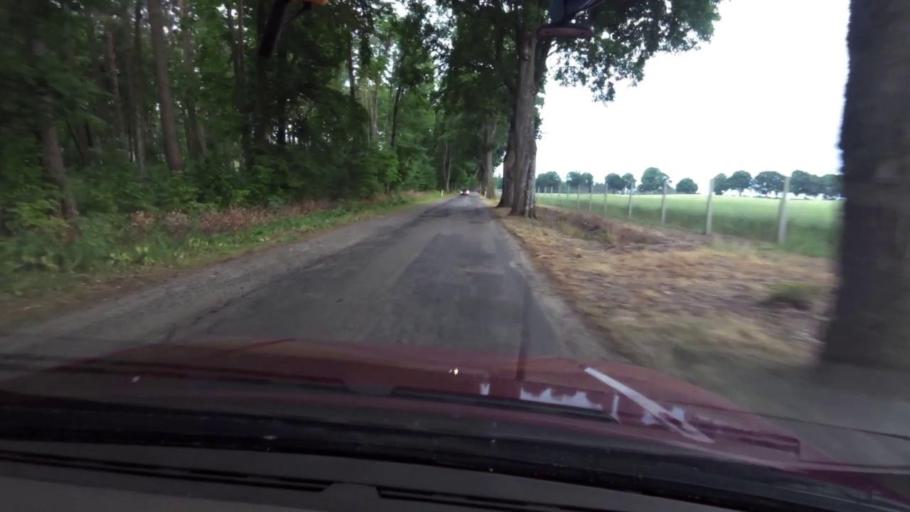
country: PL
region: Pomeranian Voivodeship
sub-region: Powiat slupski
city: Kepice
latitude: 54.2015
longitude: 16.8152
